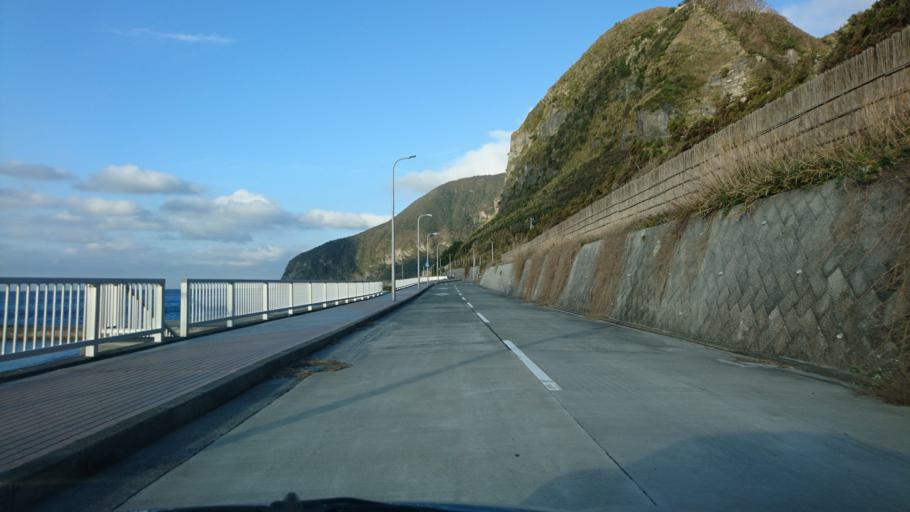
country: JP
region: Shizuoka
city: Shimoda
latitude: 34.3817
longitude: 139.2551
